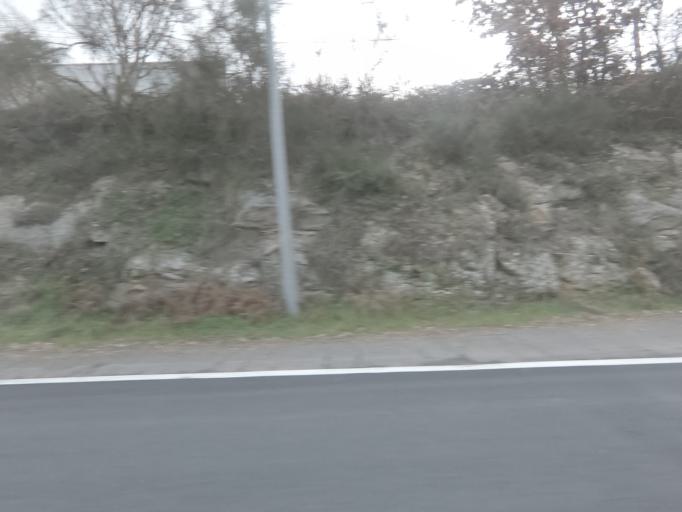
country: ES
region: Galicia
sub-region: Provincia de Ourense
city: Allariz
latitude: 42.1964
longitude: -7.7994
